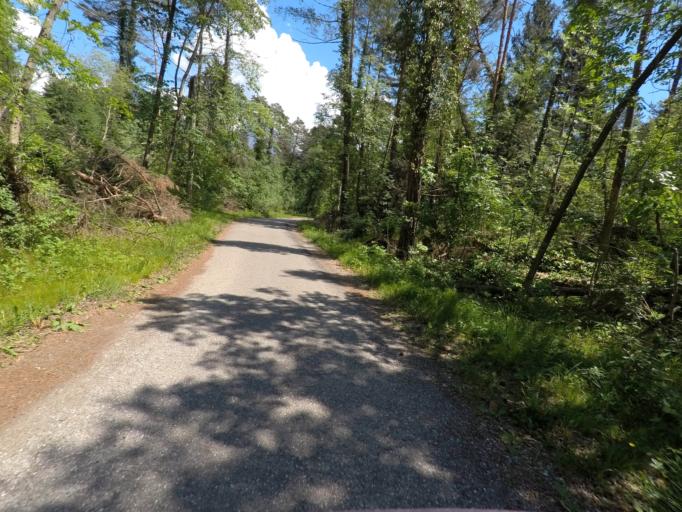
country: IT
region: Friuli Venezia Giulia
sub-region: Provincia di Udine
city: Chiaulis
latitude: 46.4040
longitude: 12.9881
